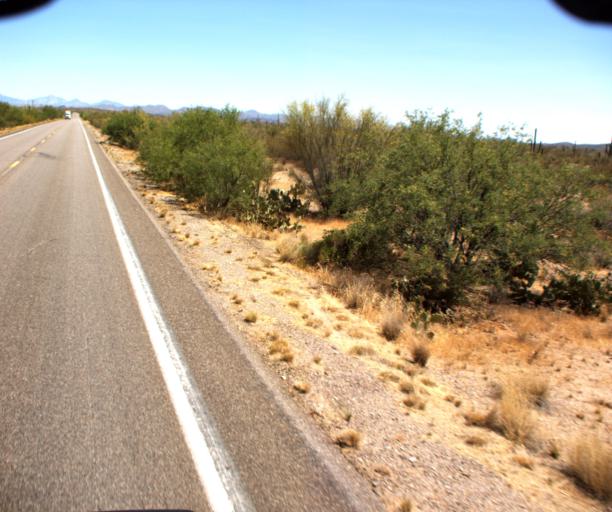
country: US
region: Arizona
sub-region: Pima County
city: Catalina
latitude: 32.7171
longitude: -111.1049
